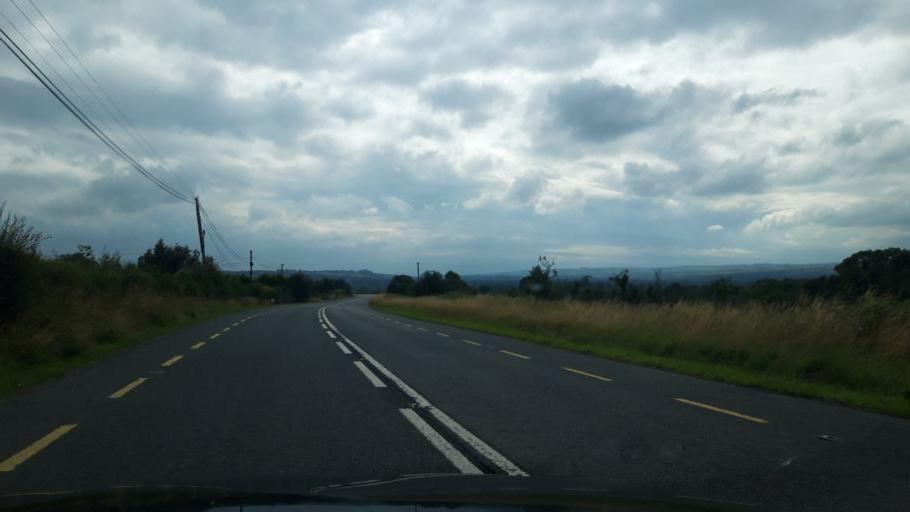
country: IE
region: Leinster
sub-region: Kilkenny
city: Castlecomer
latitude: 52.8586
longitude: -7.1137
